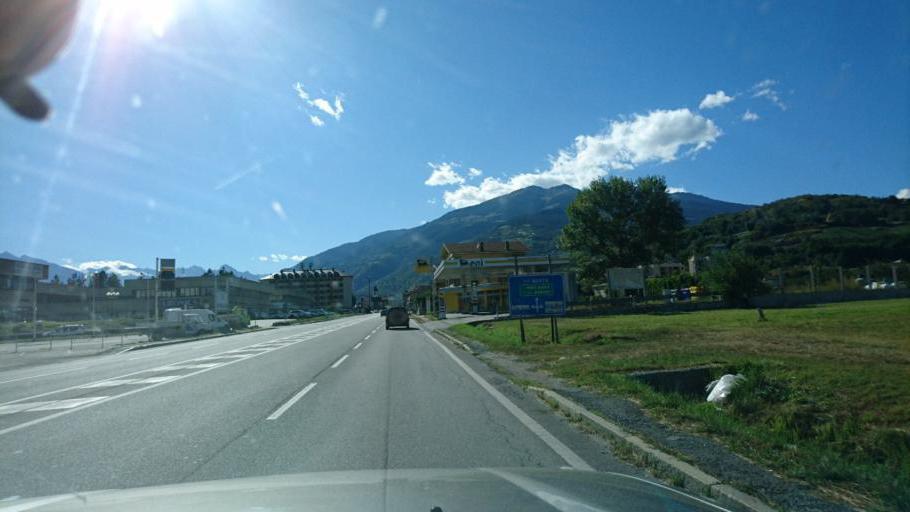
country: IT
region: Aosta Valley
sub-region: Valle d'Aosta
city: Chef-Lieu
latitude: 45.7399
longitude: 7.3514
